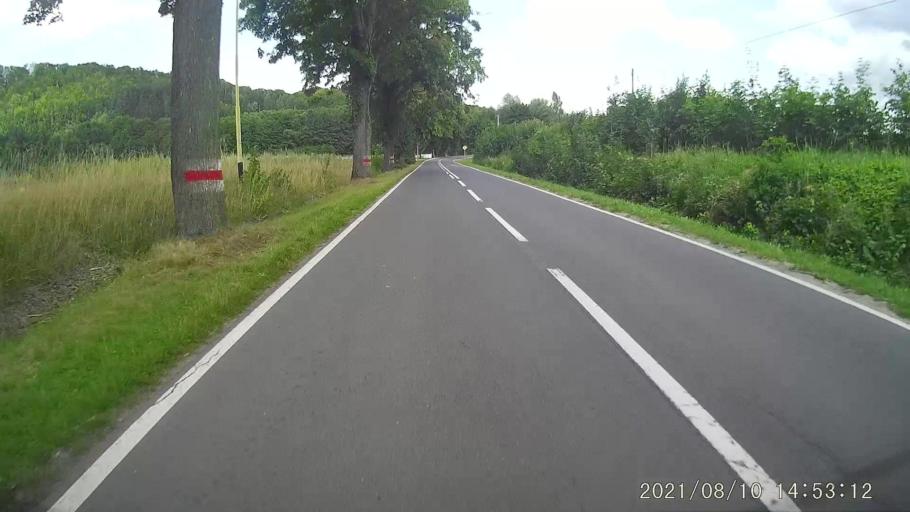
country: PL
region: Lower Silesian Voivodeship
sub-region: Powiat klodzki
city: Radkow
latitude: 50.4976
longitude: 16.3794
